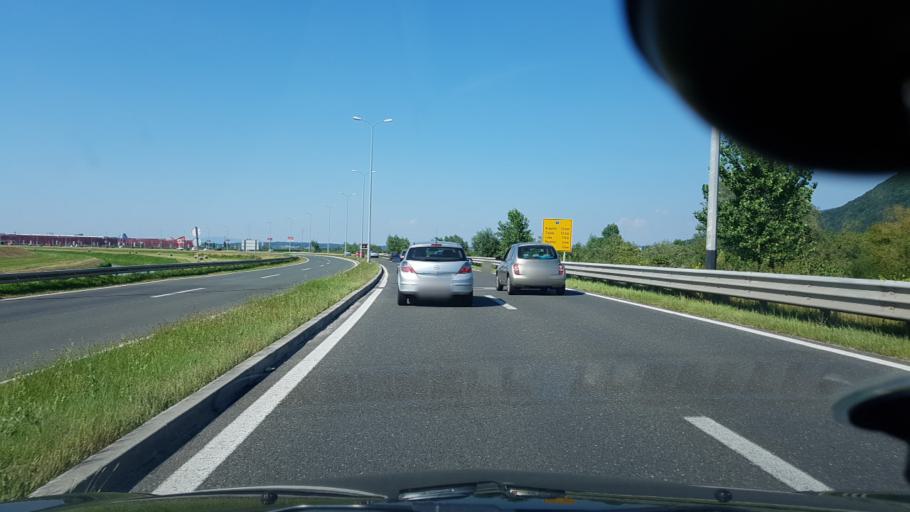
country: HR
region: Zagrebacka
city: Zapresic
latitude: 45.8594
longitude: 15.8267
